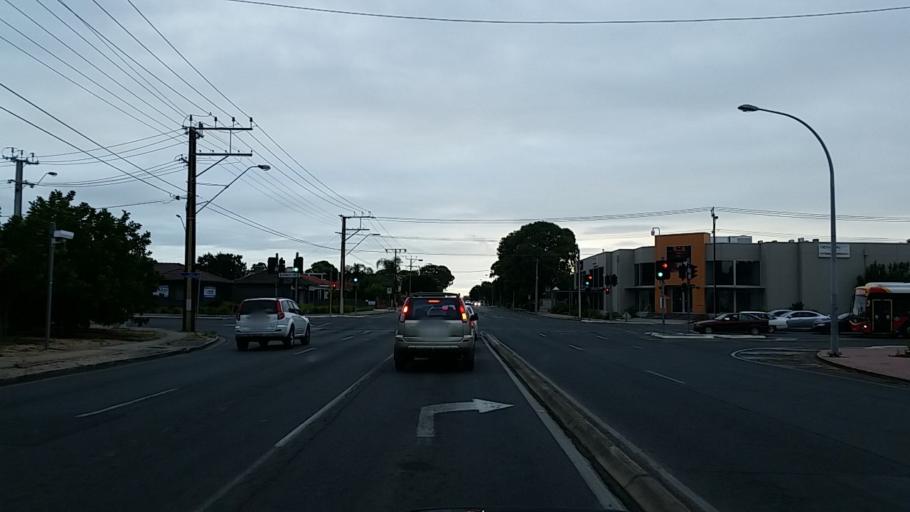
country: AU
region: South Australia
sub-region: Campbelltown
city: Paradise
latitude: -34.8733
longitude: 138.6694
